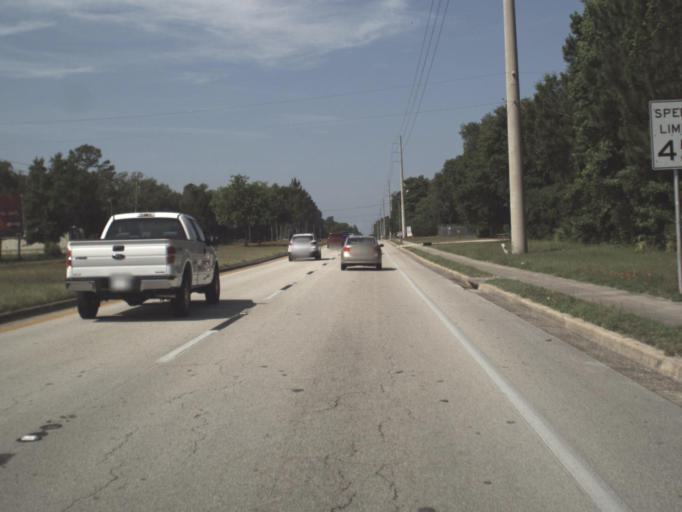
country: US
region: Florida
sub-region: Saint Johns County
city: Saint Augustine South
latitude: 29.8445
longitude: -81.3635
